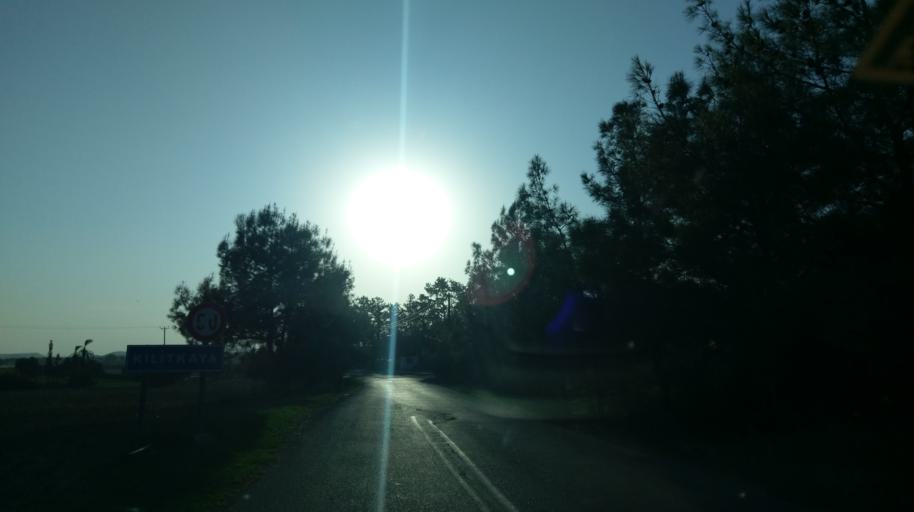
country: CY
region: Ammochostos
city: Trikomo
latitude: 35.3964
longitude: 33.9775
